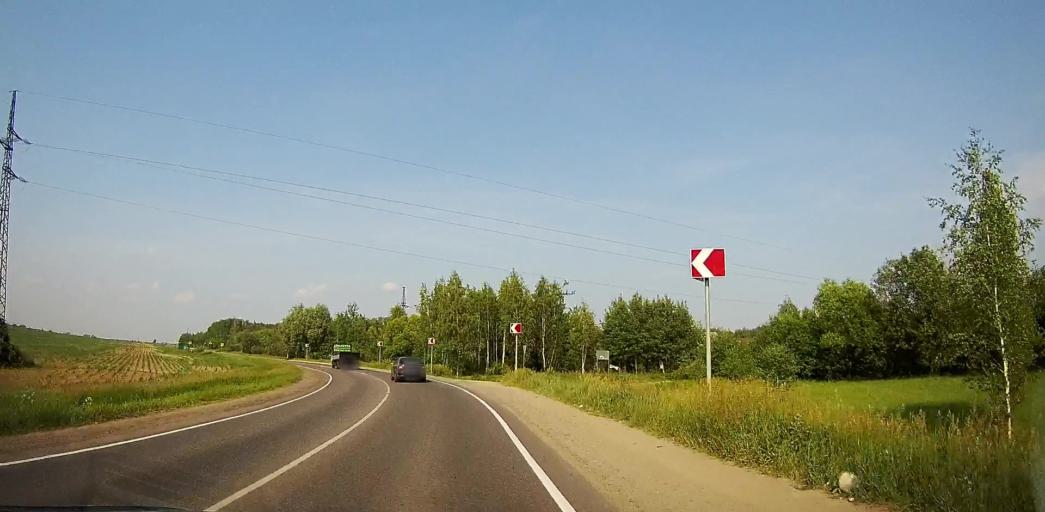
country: RU
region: Moskovskaya
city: Zhitnevo
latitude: 55.3265
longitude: 37.9012
